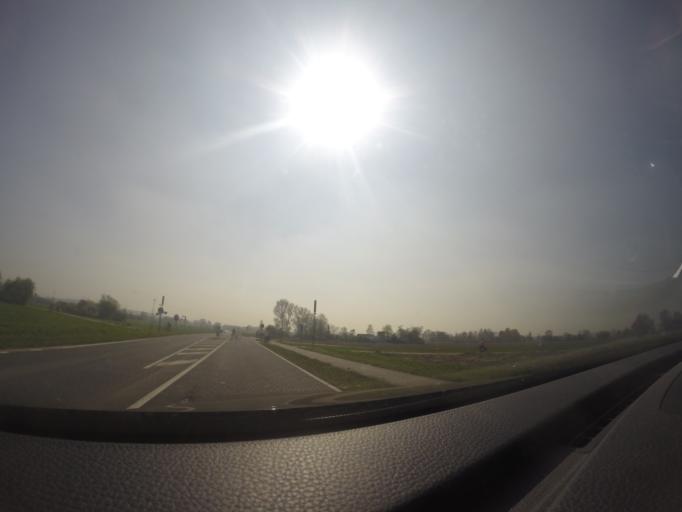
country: DE
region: North Rhine-Westphalia
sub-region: Regierungsbezirk Dusseldorf
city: Xanten
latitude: 51.6685
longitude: 6.4335
